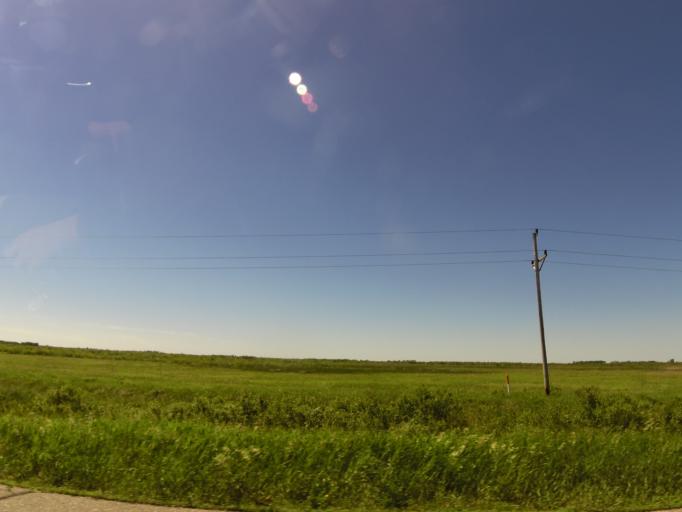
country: US
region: Minnesota
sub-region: Red Lake County
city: Red Lake Falls
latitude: 47.7603
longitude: -96.3612
